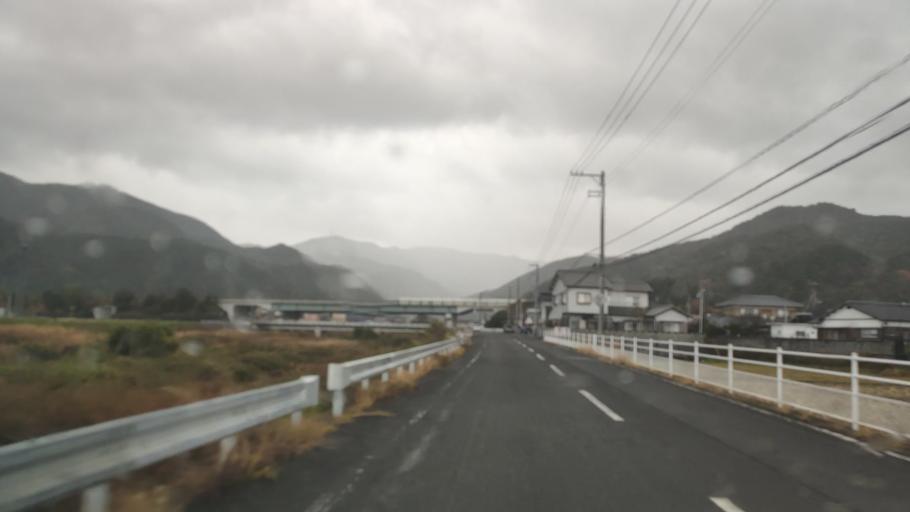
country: JP
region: Tokushima
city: Ishii
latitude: 34.2096
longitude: 134.4044
